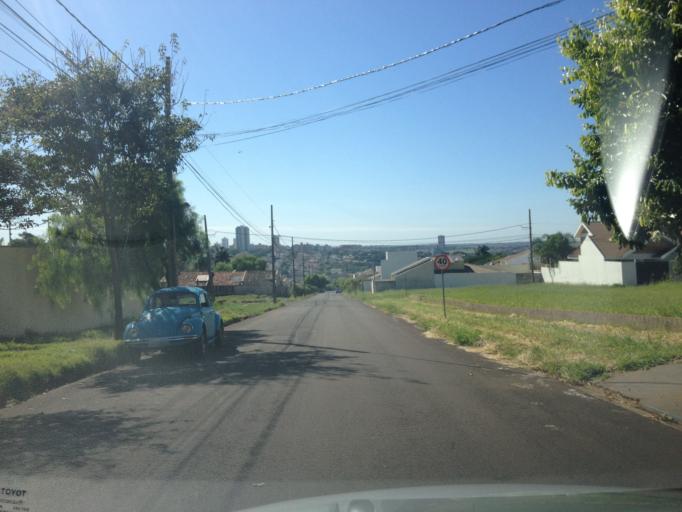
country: BR
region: Parana
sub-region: Maringa
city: Maringa
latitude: -23.4473
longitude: -51.9481
